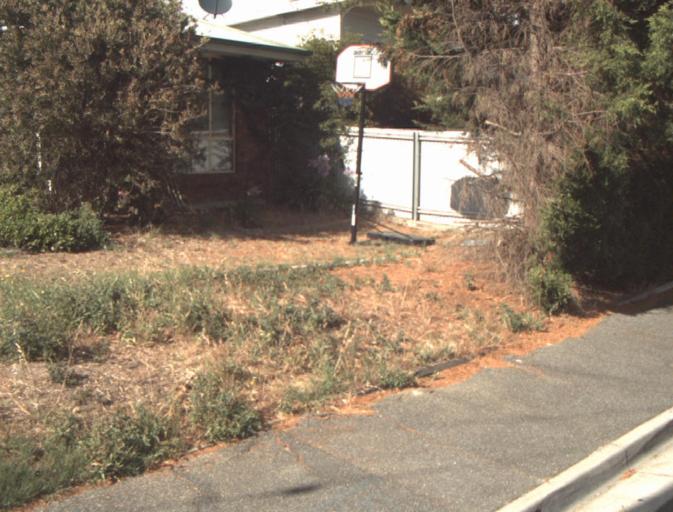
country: AU
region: Tasmania
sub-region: Launceston
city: Newstead
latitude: -41.4612
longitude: 147.1730
